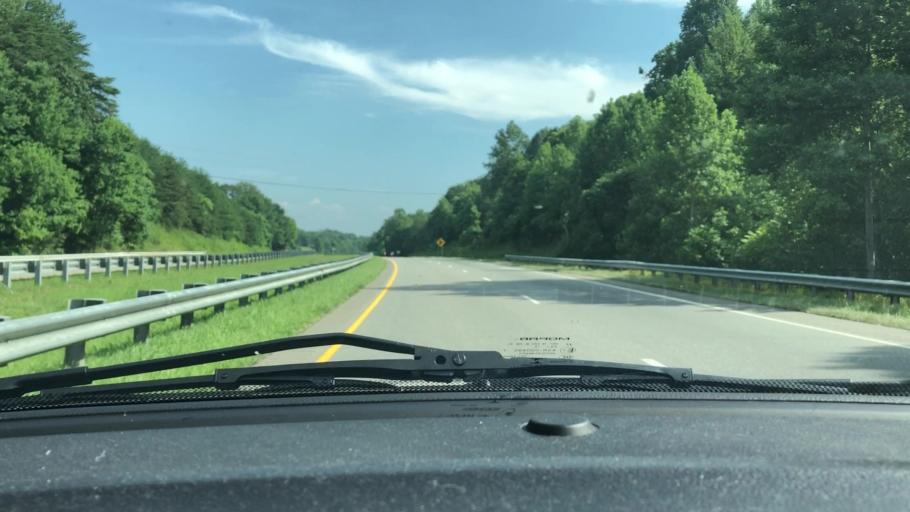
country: US
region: North Carolina
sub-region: Rockingham County
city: Stoneville
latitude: 36.5228
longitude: -79.9178
